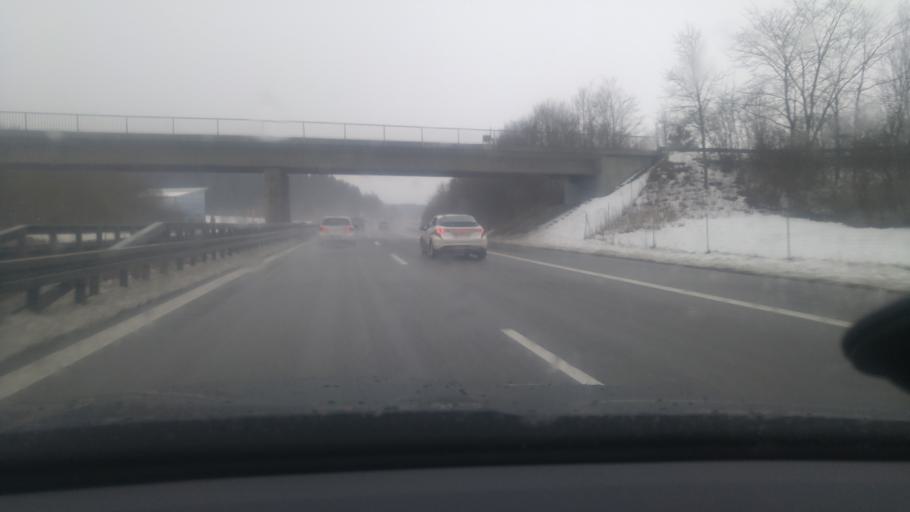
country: DE
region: Baden-Wuerttemberg
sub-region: Freiburg Region
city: Vohringen
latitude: 48.3148
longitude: 8.6445
